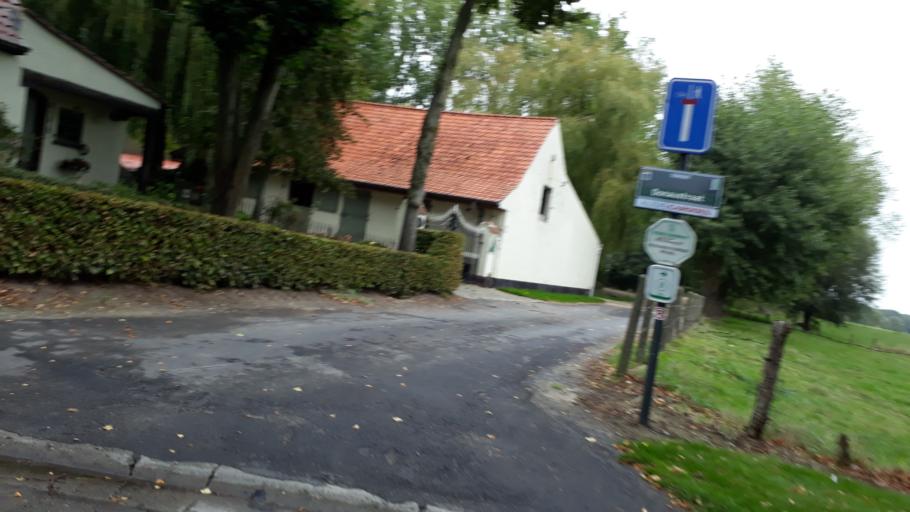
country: BE
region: Flanders
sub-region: Provincie West-Vlaanderen
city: Torhout
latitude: 51.0708
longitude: 3.1186
